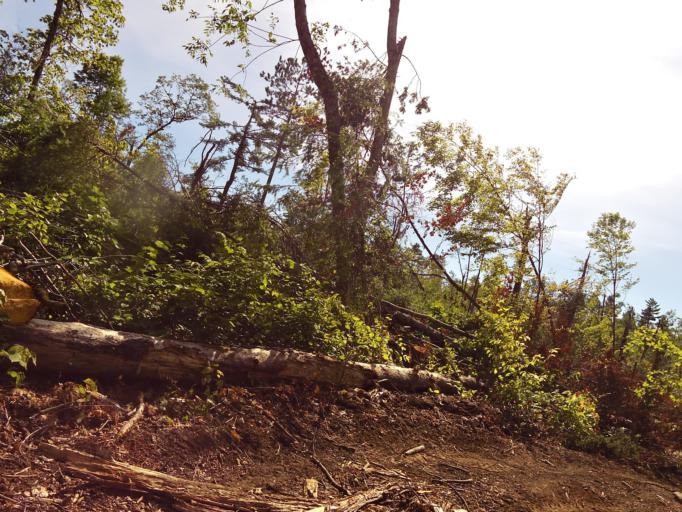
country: CA
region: Ontario
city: Renfrew
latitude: 45.1268
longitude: -76.7261
